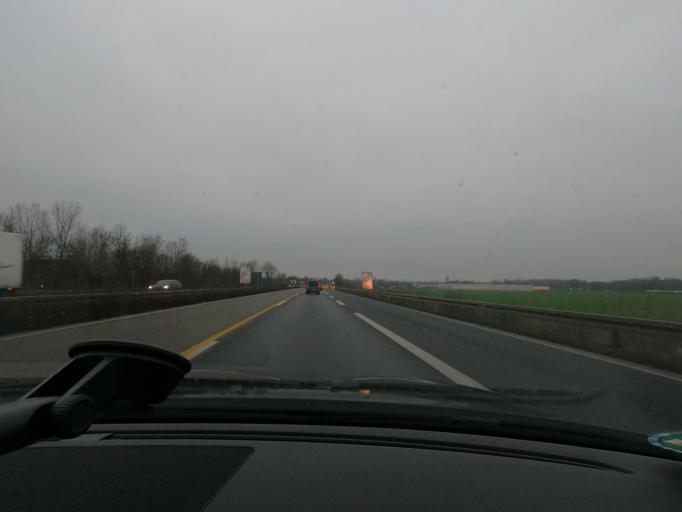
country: DE
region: North Rhine-Westphalia
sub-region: Regierungsbezirk Dusseldorf
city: Willich
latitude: 51.2703
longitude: 6.5062
